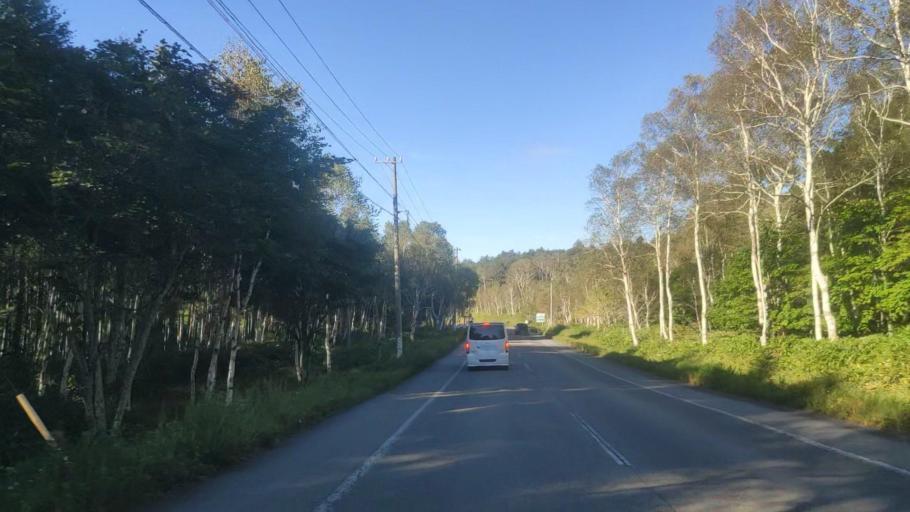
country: JP
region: Nagano
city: Kamimaruko
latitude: 36.1686
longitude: 138.2810
